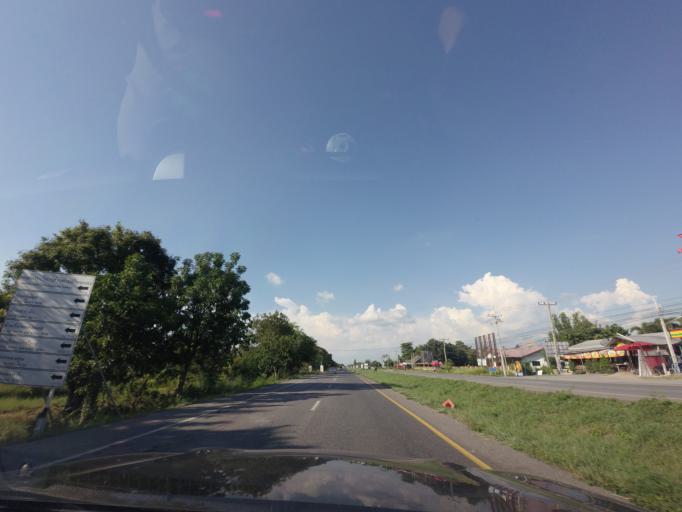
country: TH
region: Khon Kaen
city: Non Sila
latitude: 15.9976
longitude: 102.7009
